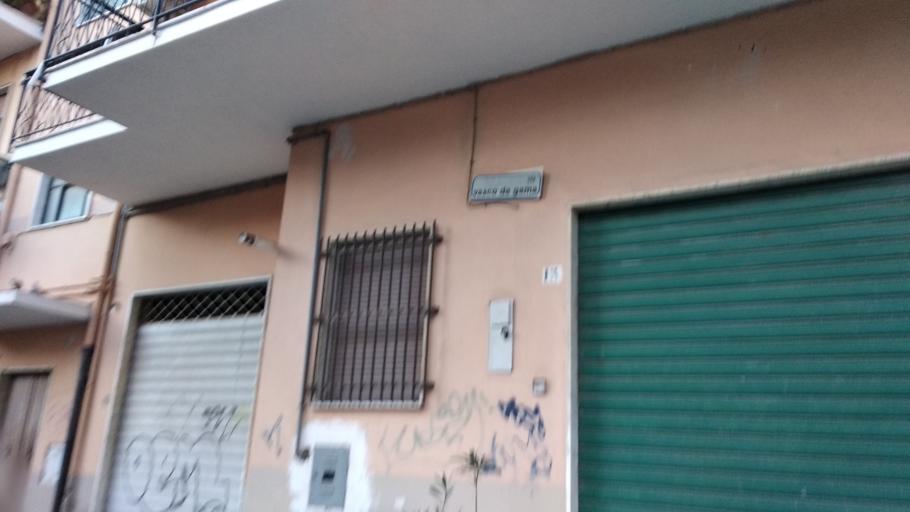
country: IT
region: Calabria
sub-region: Provincia di Catanzaro
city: Barone
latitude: 38.8280
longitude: 16.6259
